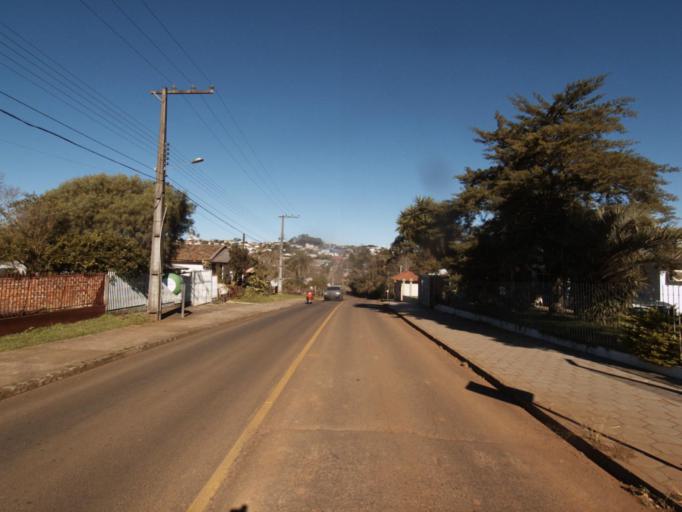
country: AR
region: Misiones
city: Bernardo de Irigoyen
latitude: -26.7131
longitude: -53.5262
